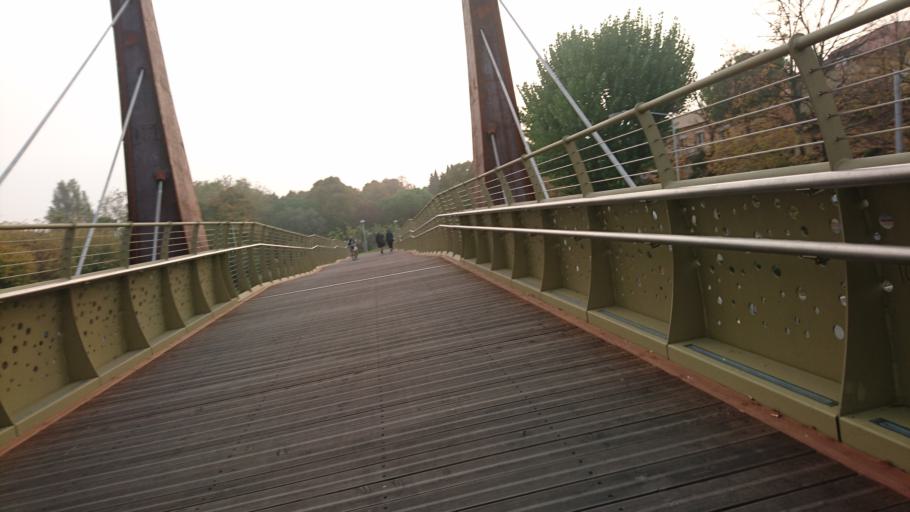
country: IT
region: Emilia-Romagna
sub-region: Provincia di Rimini
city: Rimini
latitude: 44.0596
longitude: 12.5767
